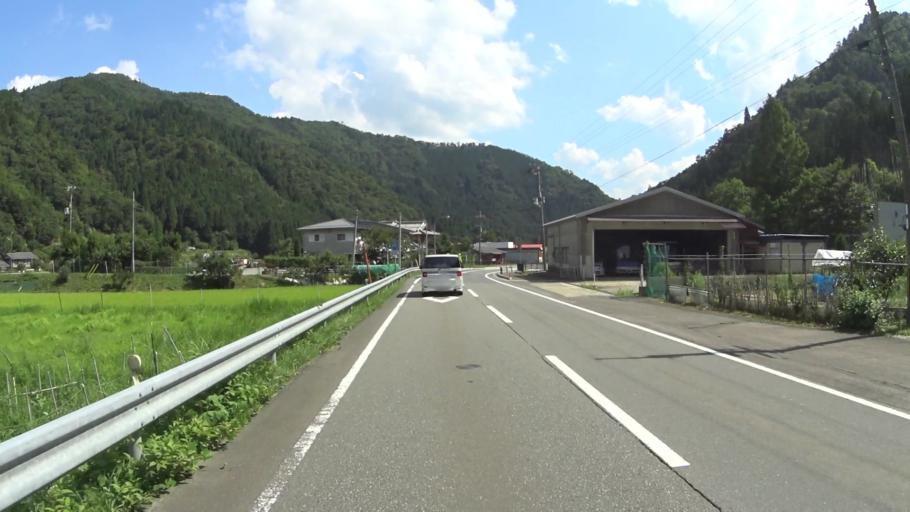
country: JP
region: Kyoto
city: Maizuru
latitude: 35.3202
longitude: 135.5556
